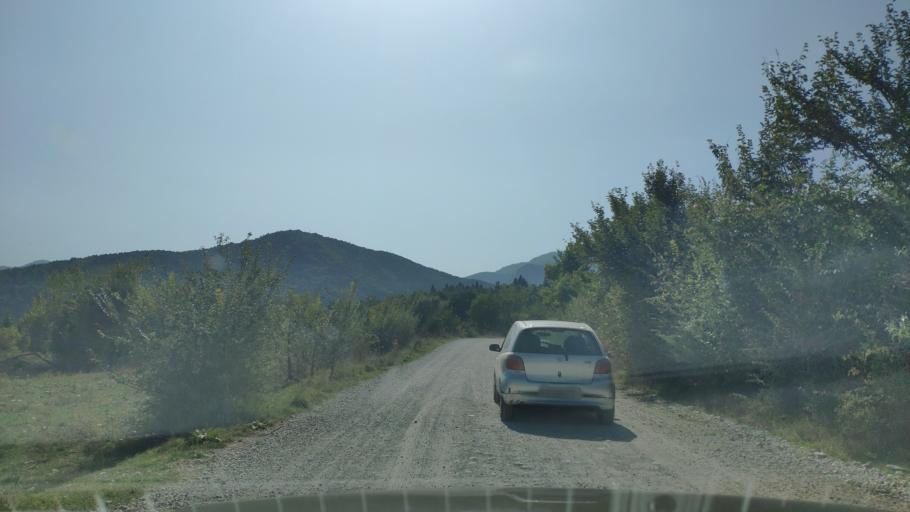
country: GR
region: West Greece
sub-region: Nomos Achaias
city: Aiyira
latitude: 37.9452
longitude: 22.3202
